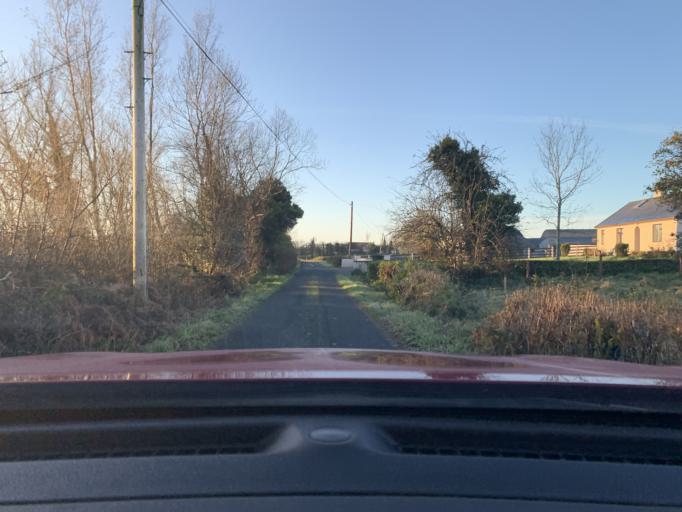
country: IE
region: Connaught
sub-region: Sligo
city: Ballymote
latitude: 54.0777
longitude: -8.5465
